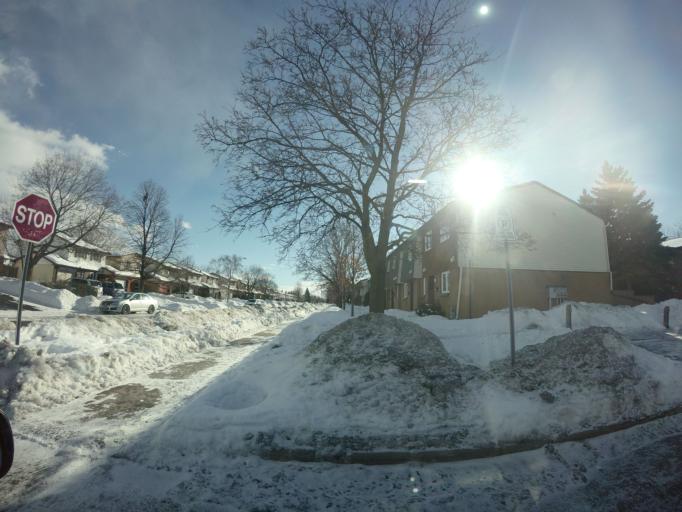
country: CA
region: Ontario
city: Ottawa
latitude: 45.4266
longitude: -75.6116
